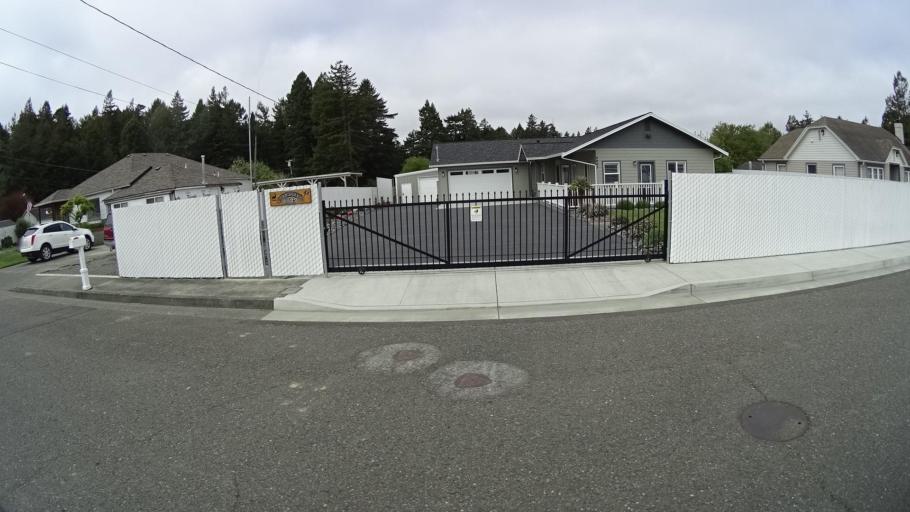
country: US
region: California
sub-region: Humboldt County
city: Cutten
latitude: 40.7627
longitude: -124.1494
